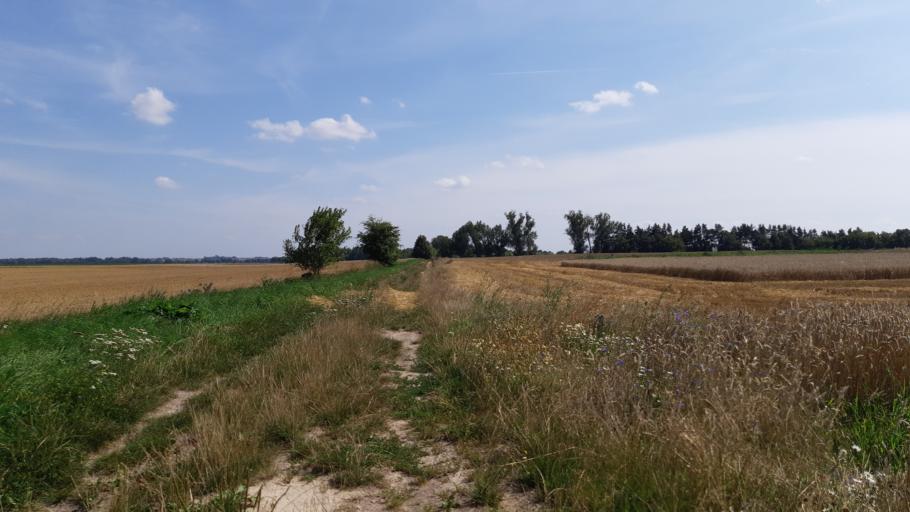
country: LT
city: Virbalis
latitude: 54.6427
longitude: 22.8186
